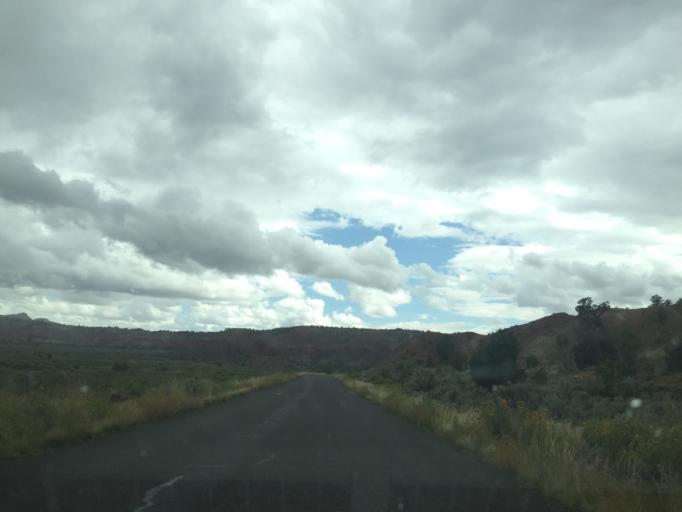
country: US
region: Utah
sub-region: Garfield County
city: Panguitch
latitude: 37.5486
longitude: -112.0464
